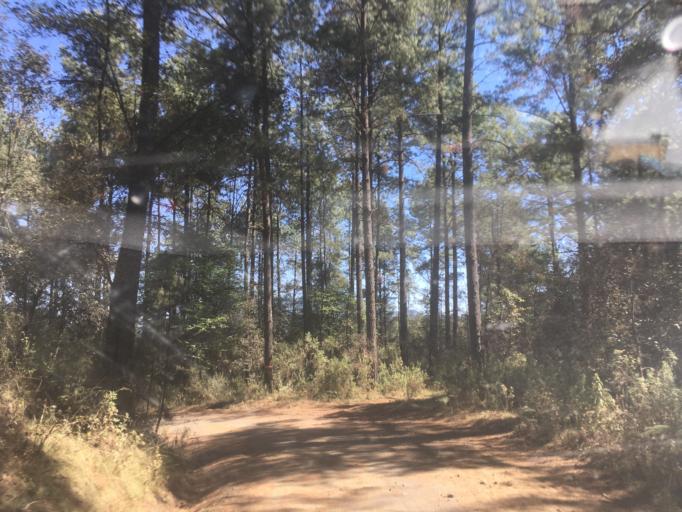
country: MX
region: Michoacan
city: Angahuan
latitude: 19.4903
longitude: -102.2054
